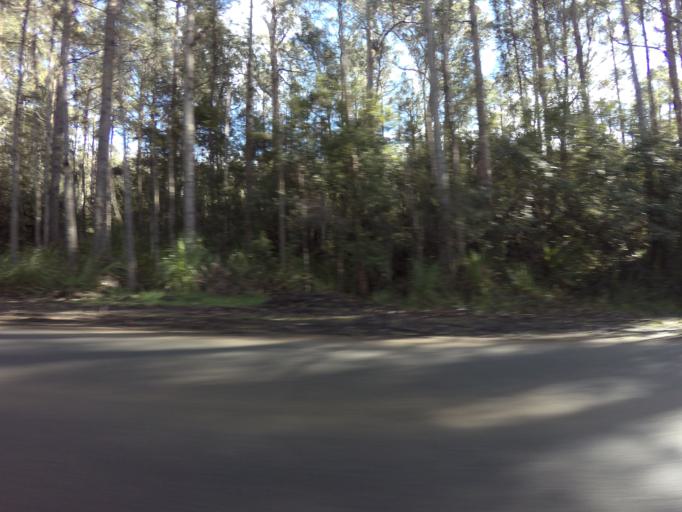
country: AU
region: Tasmania
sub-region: Huon Valley
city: Geeveston
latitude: -43.3418
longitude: 146.9662
